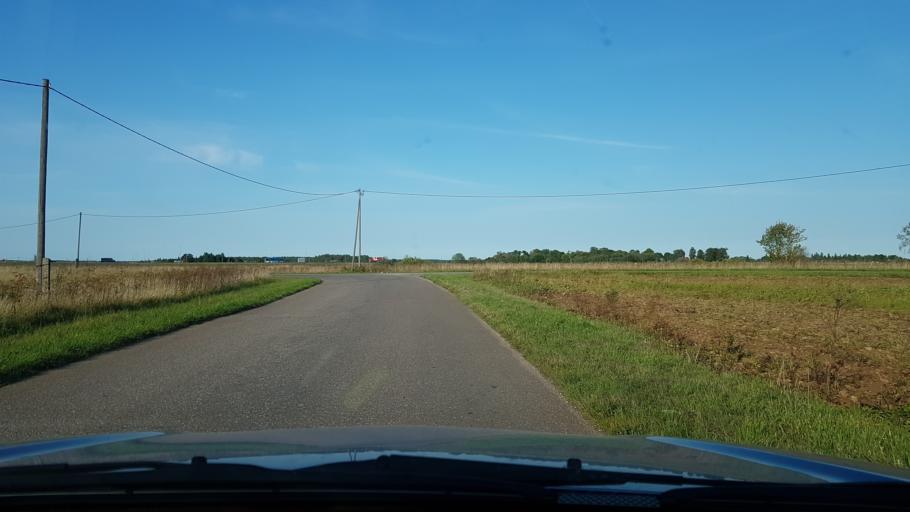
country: EE
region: Ida-Virumaa
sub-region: Narva-Joesuu linn
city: Narva-Joesuu
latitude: 59.3873
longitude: 28.0907
